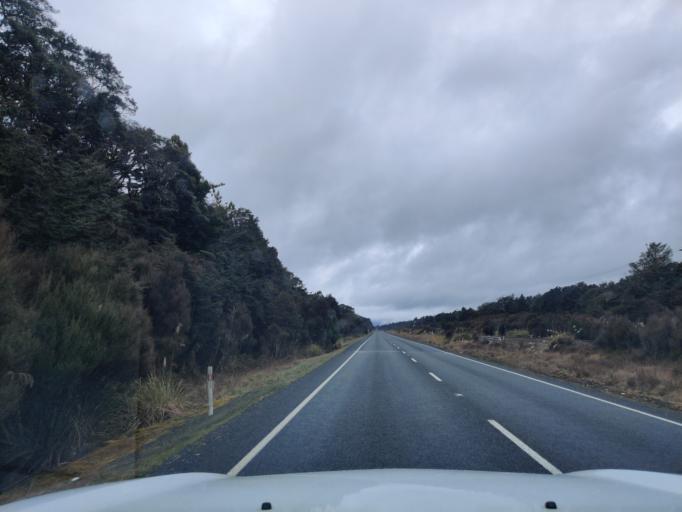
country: NZ
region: Manawatu-Wanganui
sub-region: Ruapehu District
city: Waiouru
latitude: -39.3183
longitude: 175.3866
